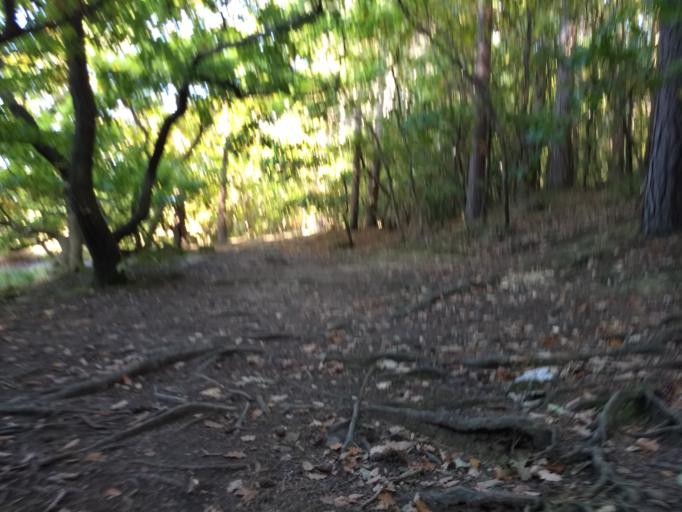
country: GB
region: England
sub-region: Isle of Wight
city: Newchurch
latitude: 50.7166
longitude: -1.2191
